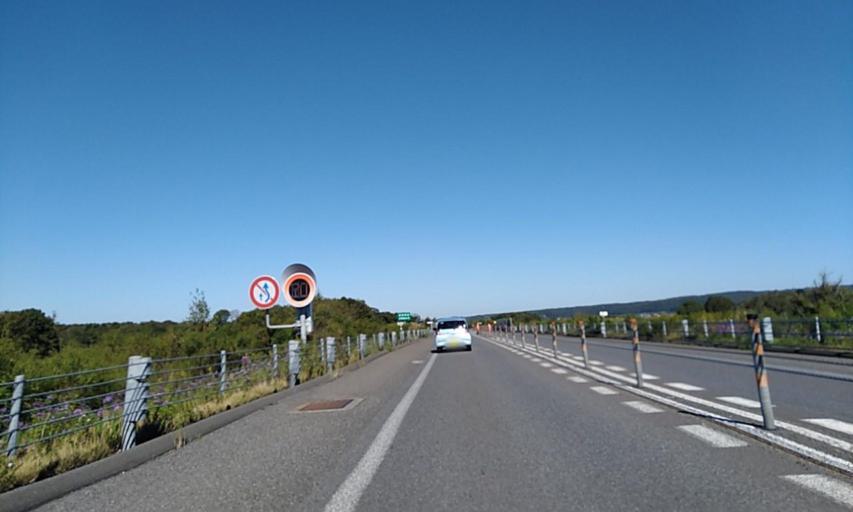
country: JP
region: Hokkaido
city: Tomakomai
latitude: 42.5632
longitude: 141.9811
